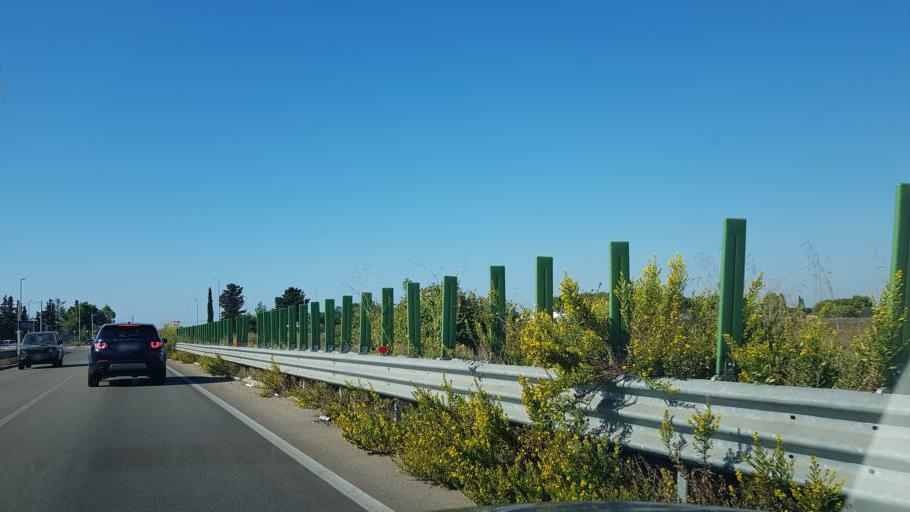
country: IT
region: Apulia
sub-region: Provincia di Lecce
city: Porto Cesareo
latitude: 40.2696
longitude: 17.9195
